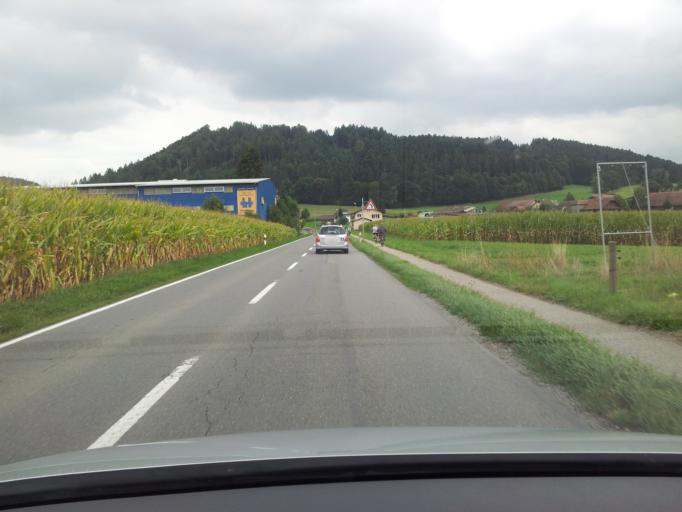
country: CH
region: Lucerne
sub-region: Willisau District
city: Ettiswil
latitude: 47.1540
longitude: 8.0315
